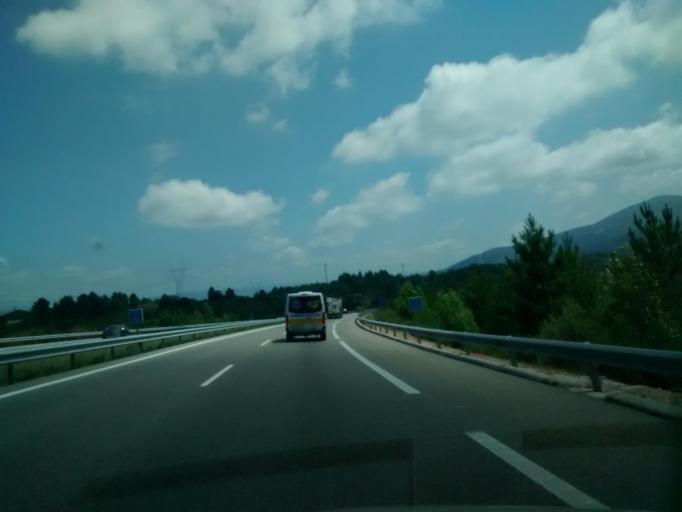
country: ES
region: Castille and Leon
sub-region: Provincia de Leon
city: Molinaseca
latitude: 42.5691
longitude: -6.5446
